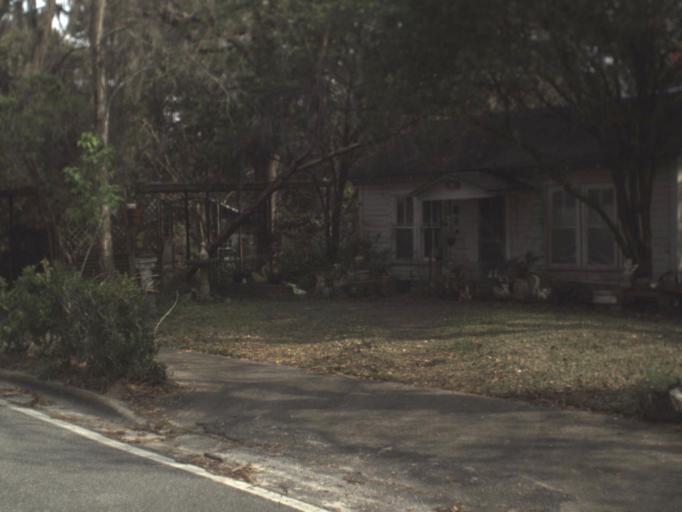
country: US
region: Florida
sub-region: Jefferson County
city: Monticello
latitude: 30.5451
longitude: -83.8548
